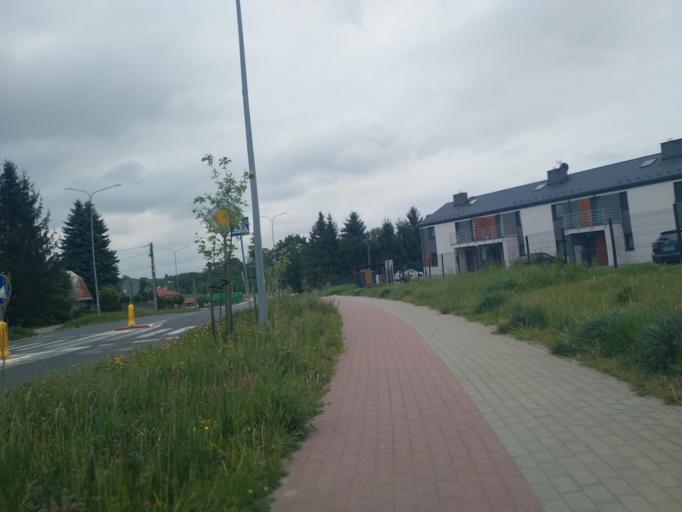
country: PL
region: Subcarpathian Voivodeship
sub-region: Krosno
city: Krosno
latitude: 49.6777
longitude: 21.7602
